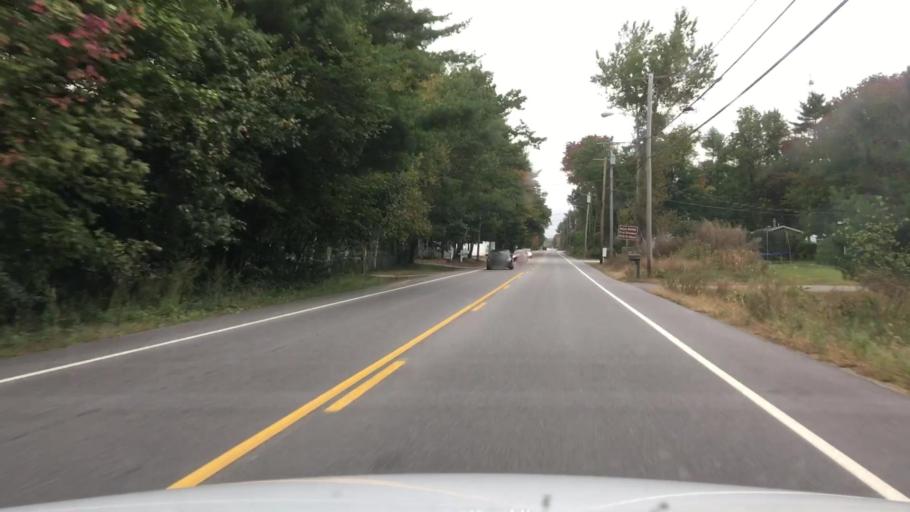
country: US
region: Maine
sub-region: Cumberland County
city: New Gloucester
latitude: 43.9258
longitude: -70.3541
